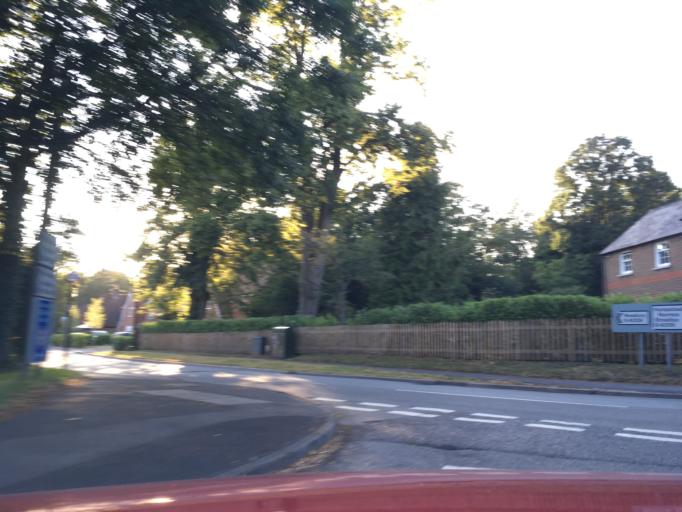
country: GB
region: England
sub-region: West Berkshire
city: Hermitage
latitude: 51.4532
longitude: -1.2732
